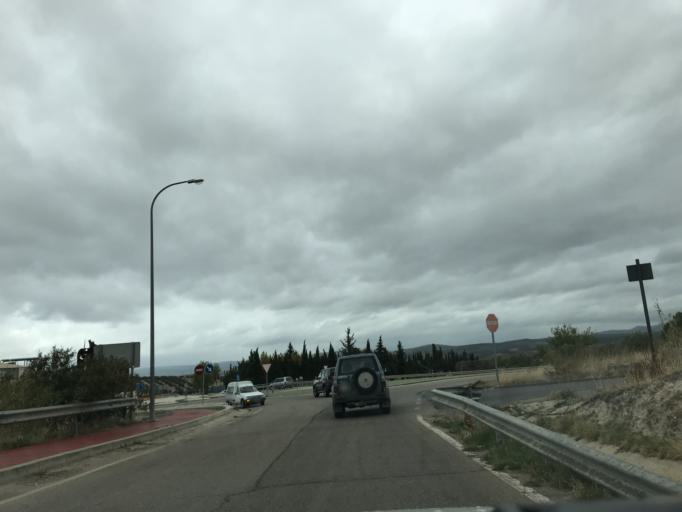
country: ES
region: Andalusia
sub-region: Provincia de Jaen
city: Peal de Becerro
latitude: 37.9178
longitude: -3.1315
